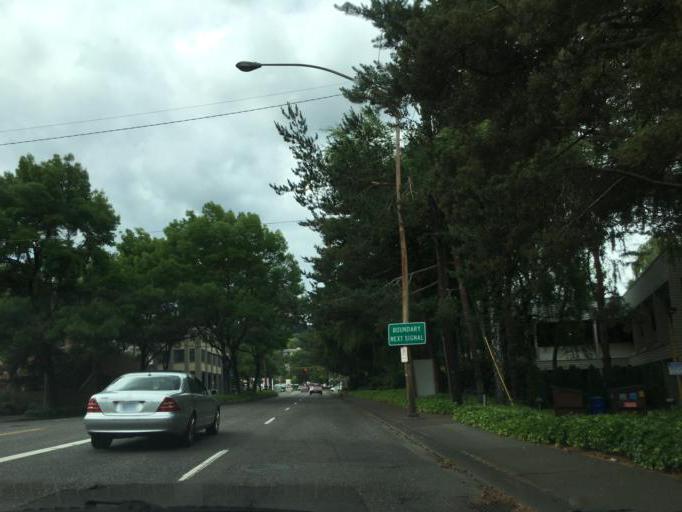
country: US
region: Oregon
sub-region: Multnomah County
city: Portland
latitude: 45.4836
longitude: -122.6743
